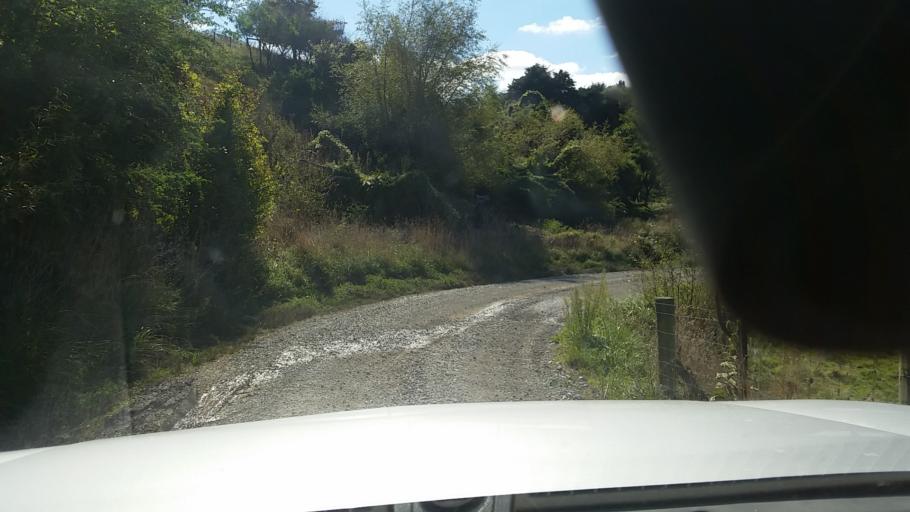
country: NZ
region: Marlborough
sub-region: Marlborough District
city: Blenheim
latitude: -41.8248
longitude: 174.1194
